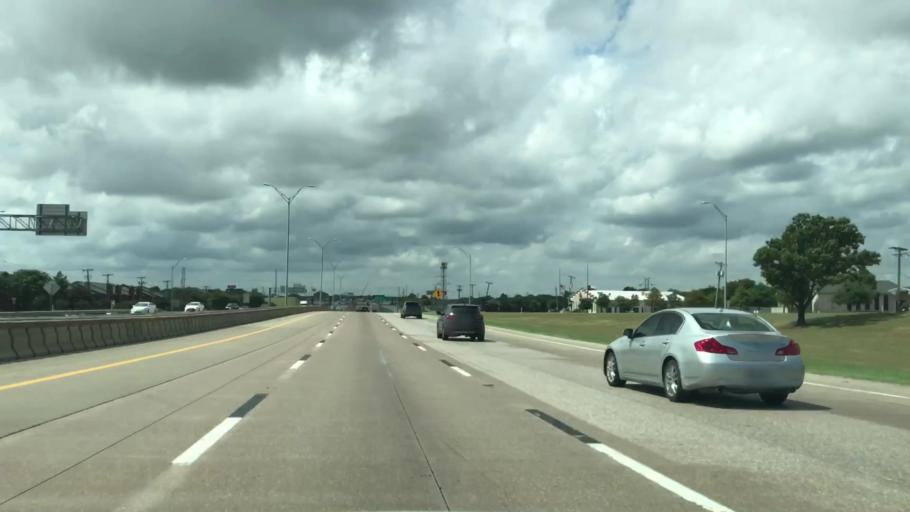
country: US
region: Texas
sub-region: Dallas County
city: Mesquite
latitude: 32.8222
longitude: -96.6328
